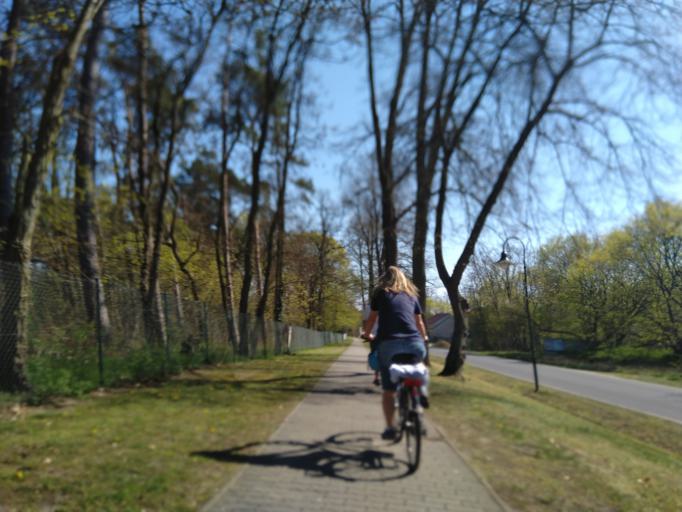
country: DE
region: Brandenburg
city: Biesenthal
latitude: 52.7688
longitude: 13.6159
